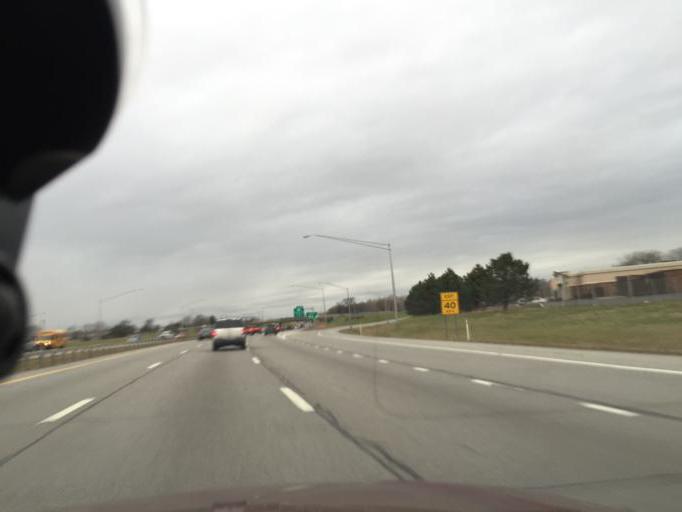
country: US
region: New York
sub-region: Monroe County
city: Rochester
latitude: 43.1280
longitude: -77.6586
